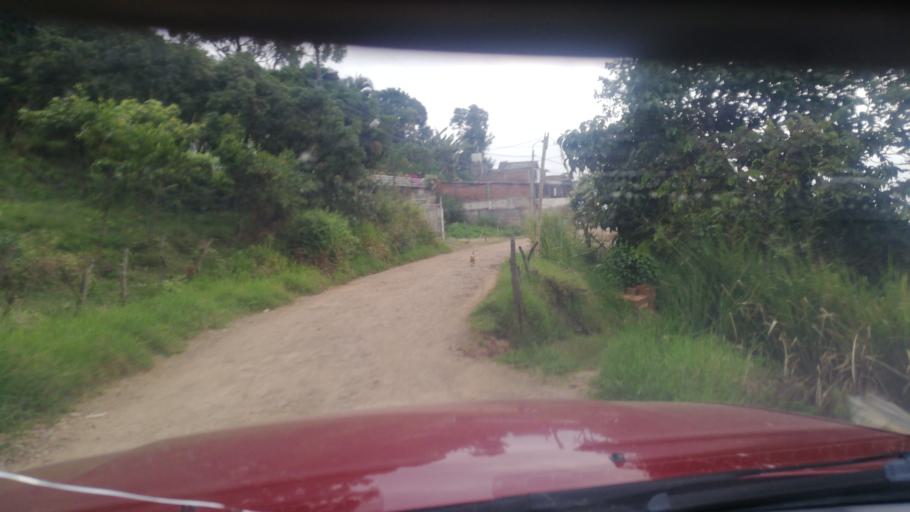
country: CO
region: Valle del Cauca
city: Cali
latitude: 3.5051
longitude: -76.5449
